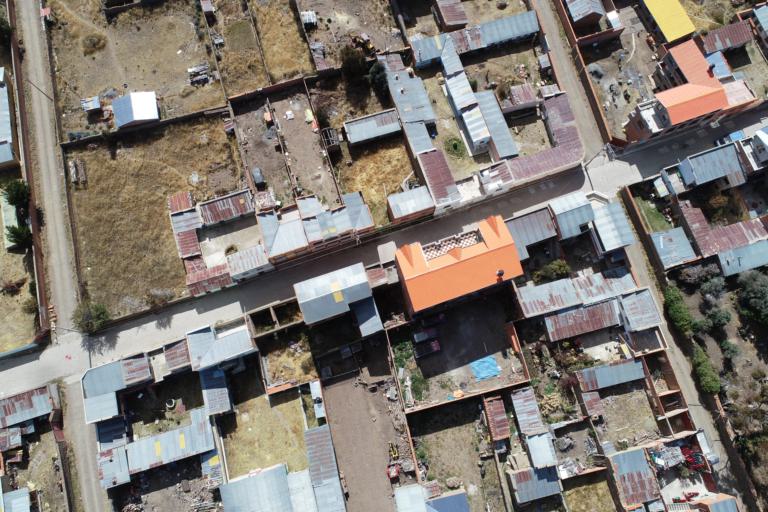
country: BO
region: La Paz
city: Achacachi
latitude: -15.8968
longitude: -68.9069
